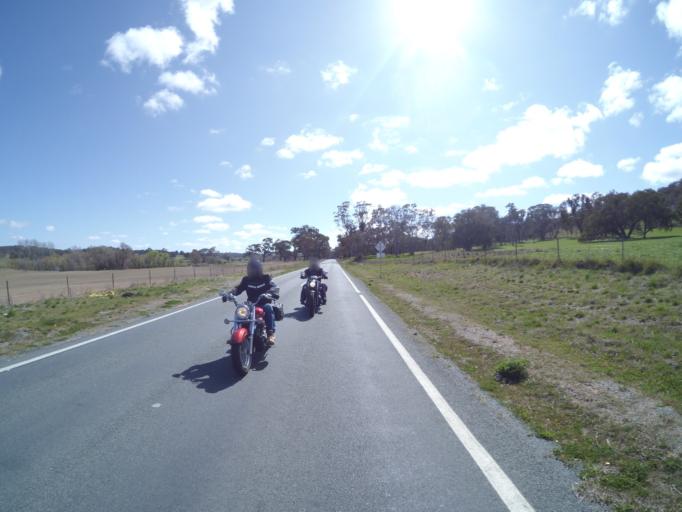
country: AU
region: New South Wales
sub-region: Queanbeyan
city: Queanbeyan
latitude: -35.3064
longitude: 149.2508
